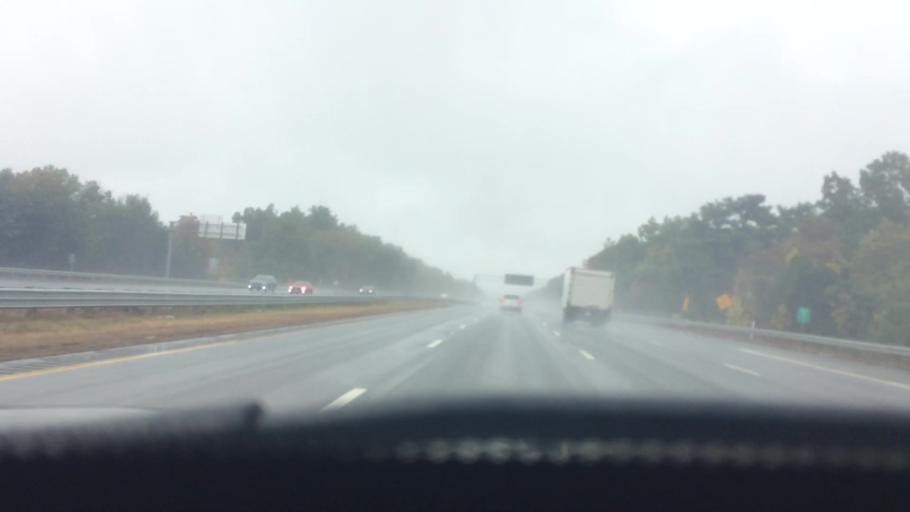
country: US
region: Massachusetts
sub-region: Middlesex County
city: Wilmington
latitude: 42.5574
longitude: -71.1400
